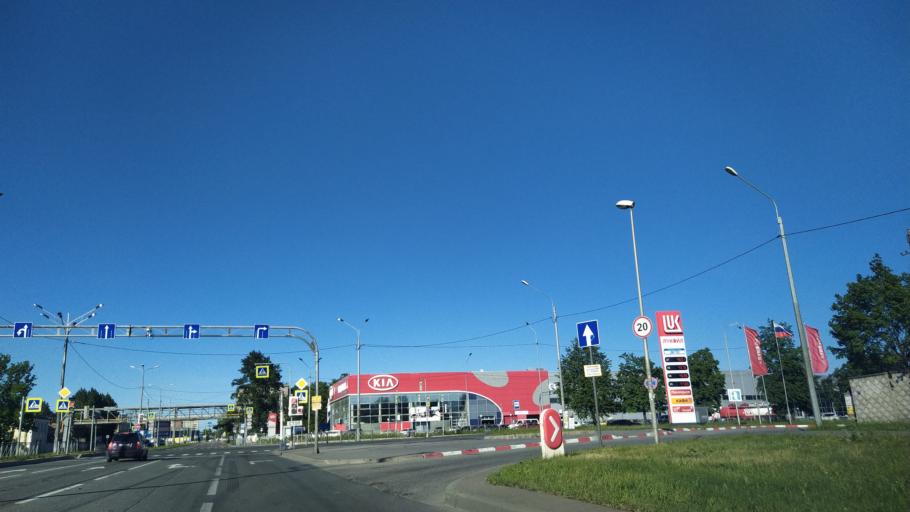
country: RU
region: St.-Petersburg
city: Kupchino
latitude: 59.8887
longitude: 30.3791
